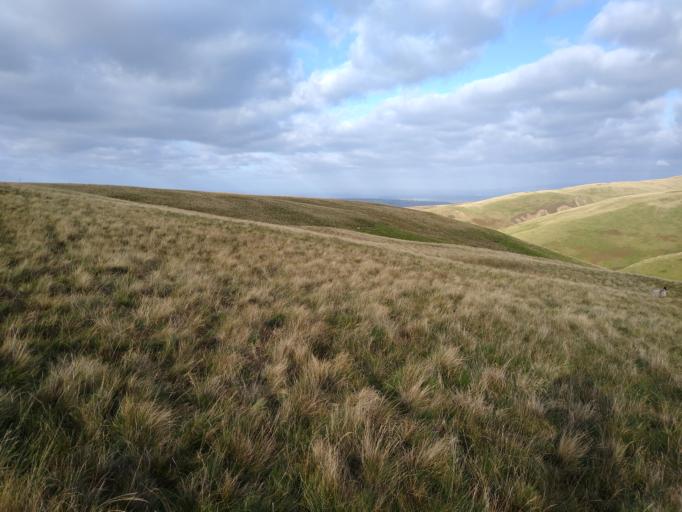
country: GB
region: England
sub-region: Cumbria
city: Keswick
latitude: 54.7076
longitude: -3.0967
